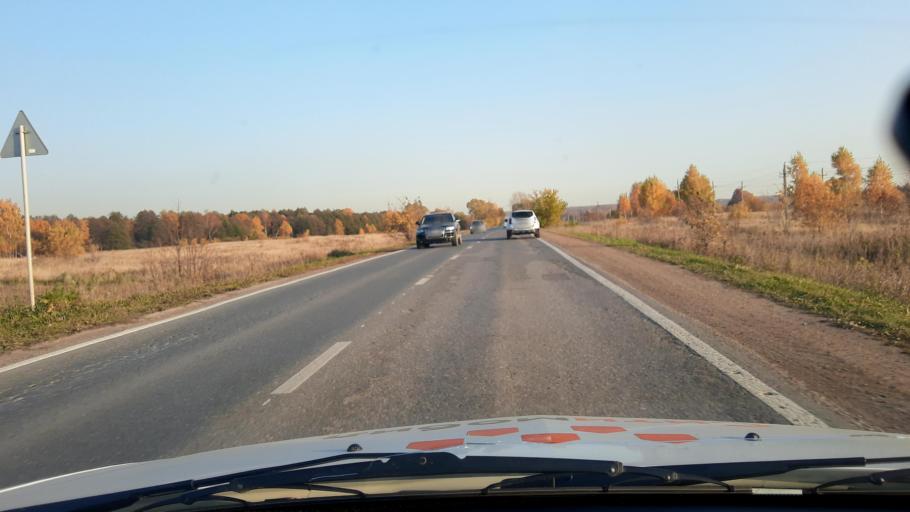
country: RU
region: Bashkortostan
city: Iglino
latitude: 54.7465
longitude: 56.2122
